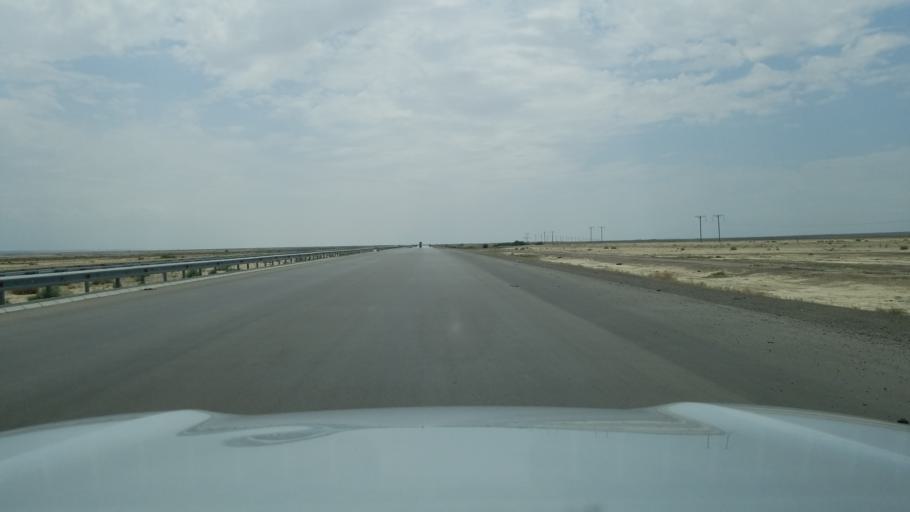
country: TM
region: Balkan
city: Gazanjyk
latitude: 39.2353
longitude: 55.0780
